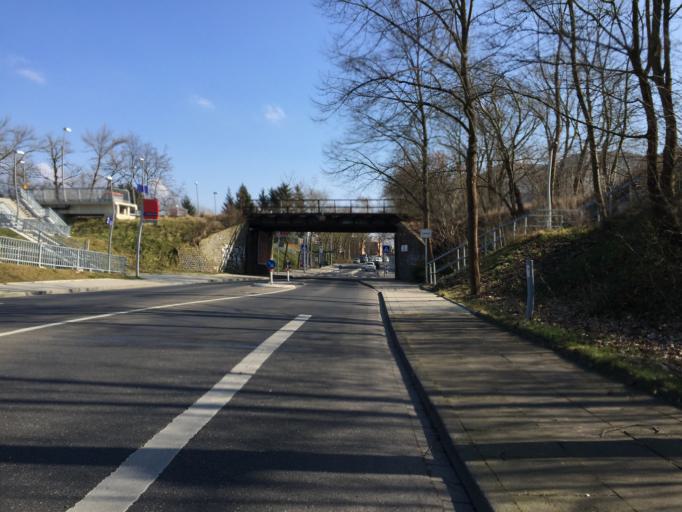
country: DE
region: North Rhine-Westphalia
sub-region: Regierungsbezirk Koln
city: Bonn
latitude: 50.7353
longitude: 7.0607
